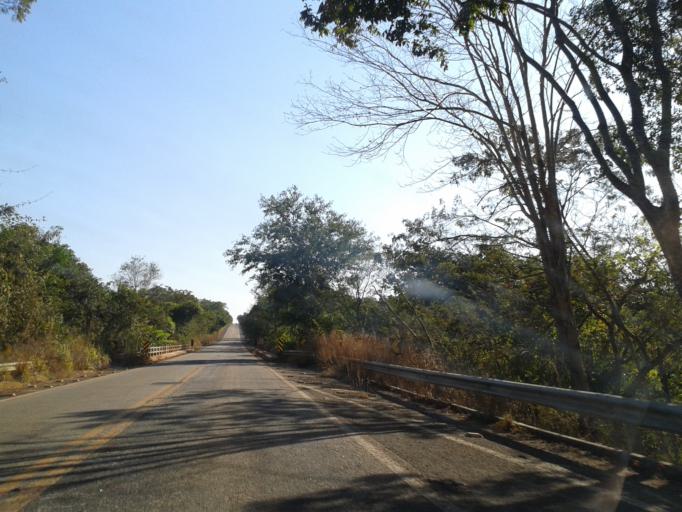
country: BR
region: Goias
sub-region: Mozarlandia
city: Mozarlandia
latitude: -14.9825
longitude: -50.5812
